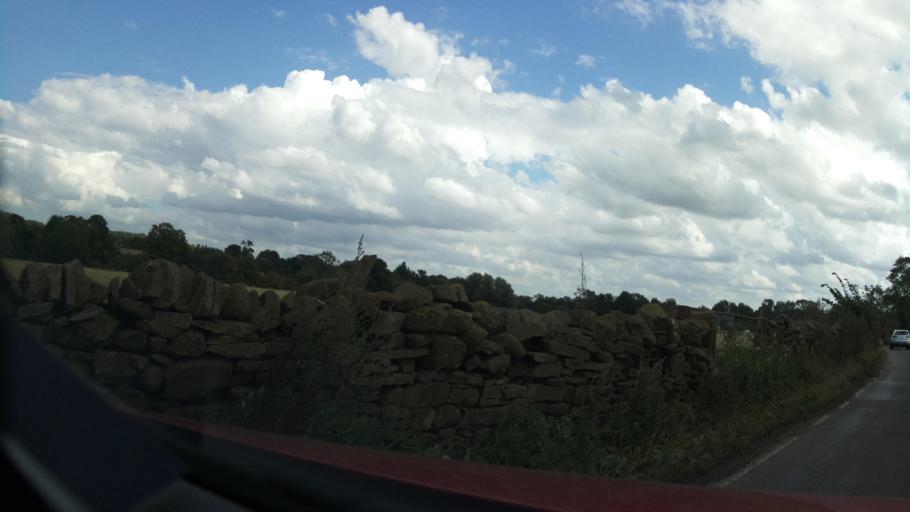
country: GB
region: England
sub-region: North Yorkshire
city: Leyburn
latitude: 54.2814
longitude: -1.7837
